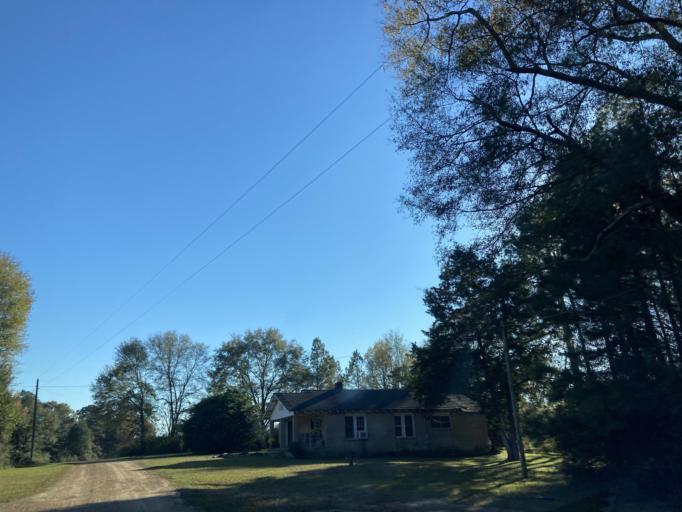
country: US
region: Mississippi
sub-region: Lamar County
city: Sumrall
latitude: 31.4003
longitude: -89.5822
